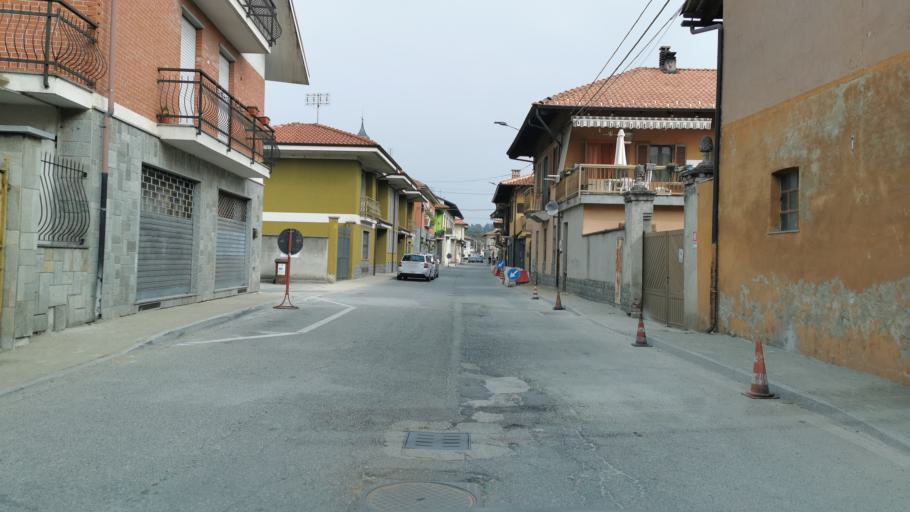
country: IT
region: Piedmont
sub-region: Provincia di Torino
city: Tonengo-Casale
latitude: 45.2861
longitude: 7.9371
